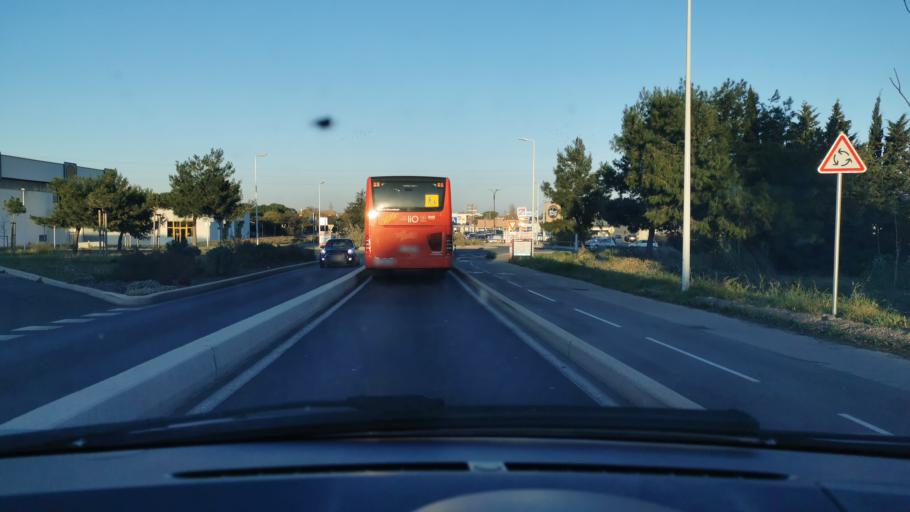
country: FR
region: Languedoc-Roussillon
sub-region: Departement de l'Herault
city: Frontignan
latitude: 43.4371
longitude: 3.7407
